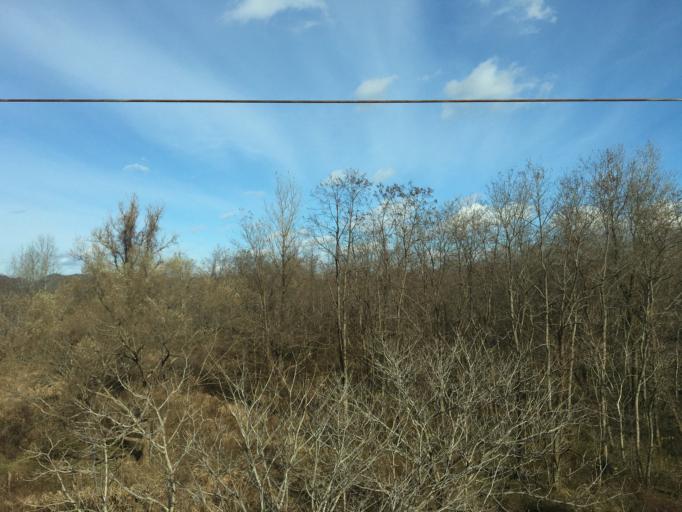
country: JP
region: Akita
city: Omagari
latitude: 39.4856
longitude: 140.4588
